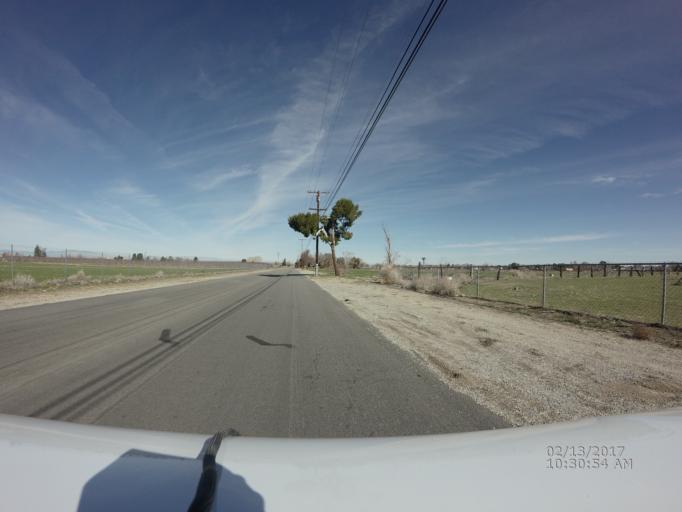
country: US
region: California
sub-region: Los Angeles County
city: Littlerock
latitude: 34.5309
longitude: -117.9793
